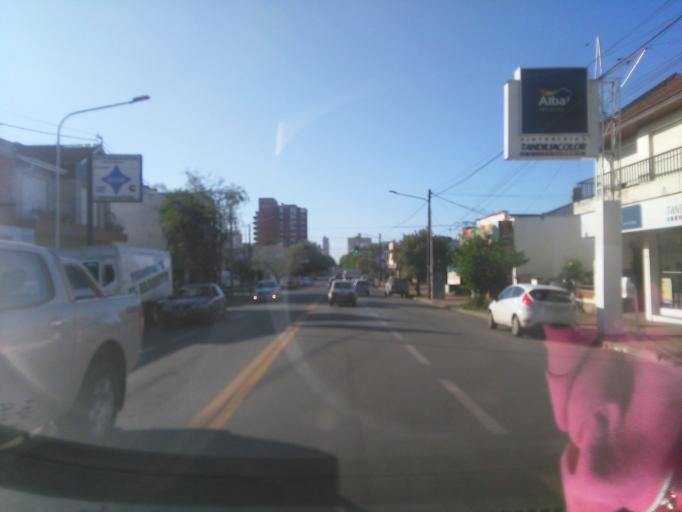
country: AR
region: Buenos Aires
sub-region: Partido de Tandil
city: Tandil
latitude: -37.3296
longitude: -59.1274
